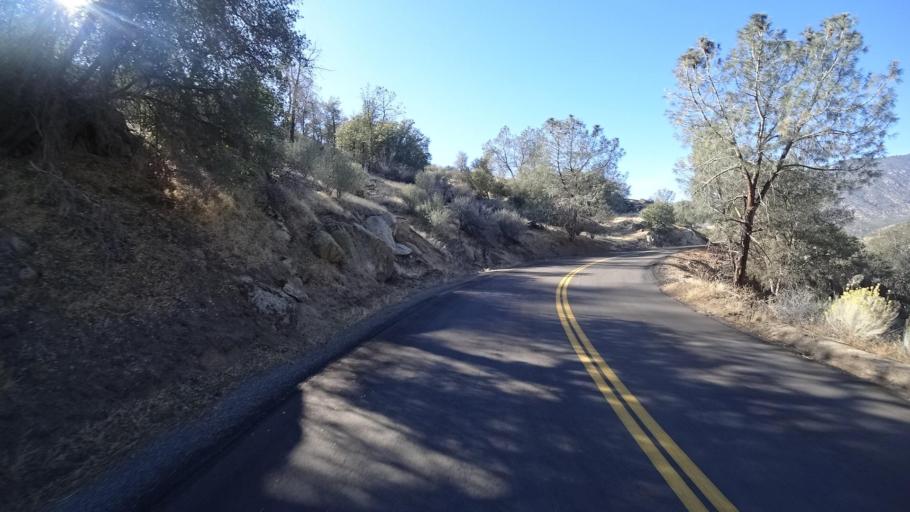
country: US
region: California
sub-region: Kern County
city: Bodfish
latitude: 35.5937
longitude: -118.5087
